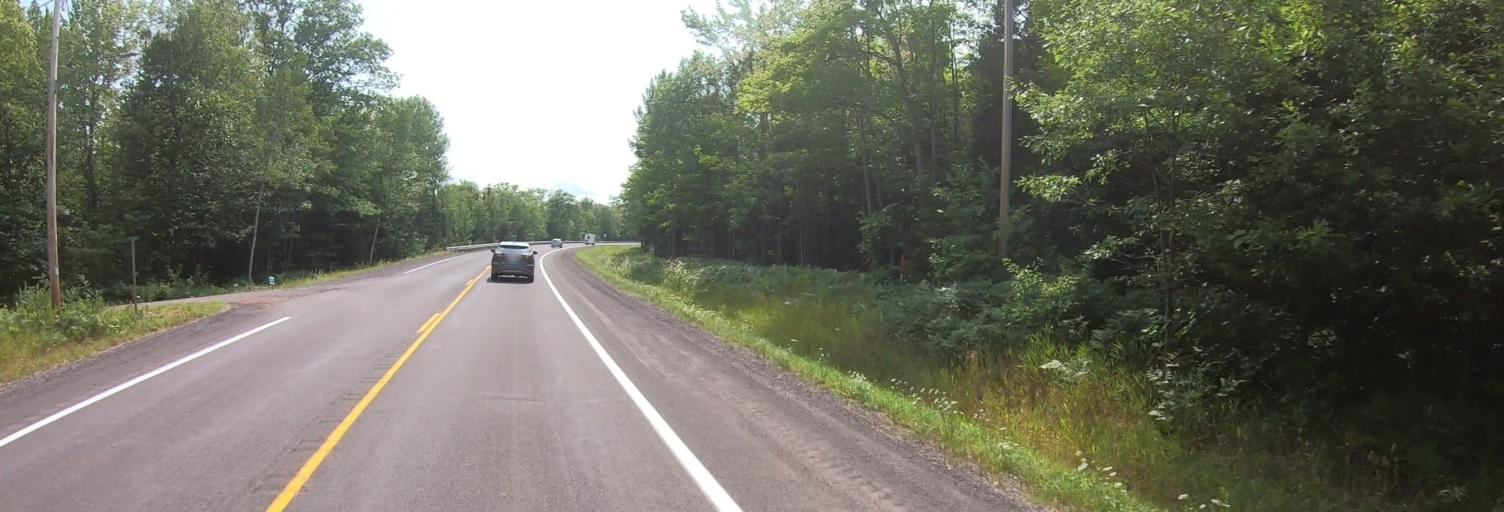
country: US
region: Michigan
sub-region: Houghton County
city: Hancock
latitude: 46.9024
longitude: -88.8397
